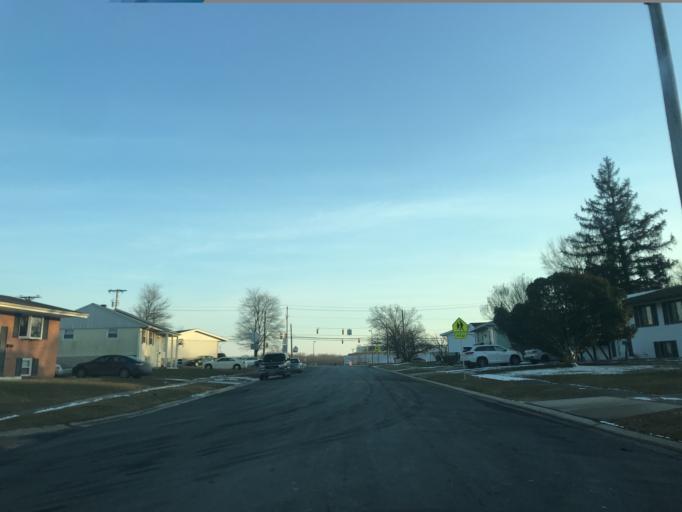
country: US
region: Maryland
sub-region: Harford County
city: Edgewood
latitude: 39.4246
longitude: -76.2914
